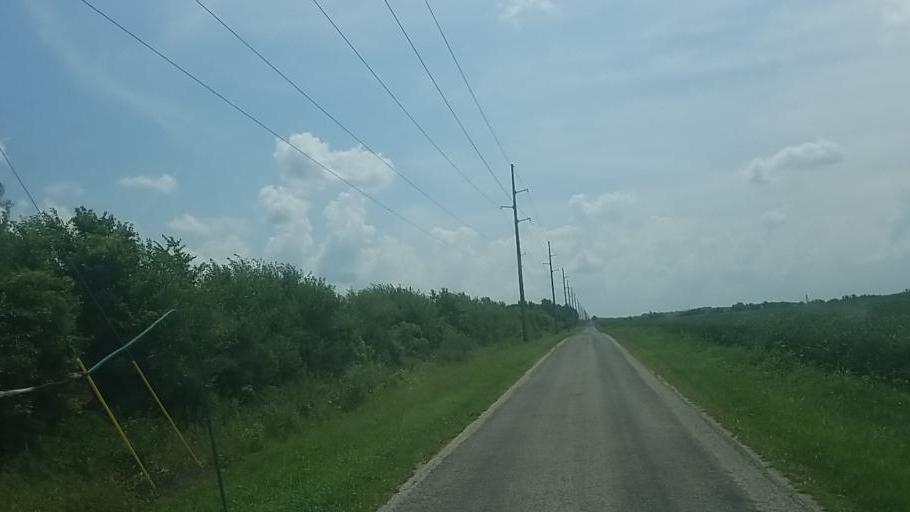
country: US
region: Ohio
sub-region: Wyandot County
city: Upper Sandusky
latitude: 40.6428
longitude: -83.3239
